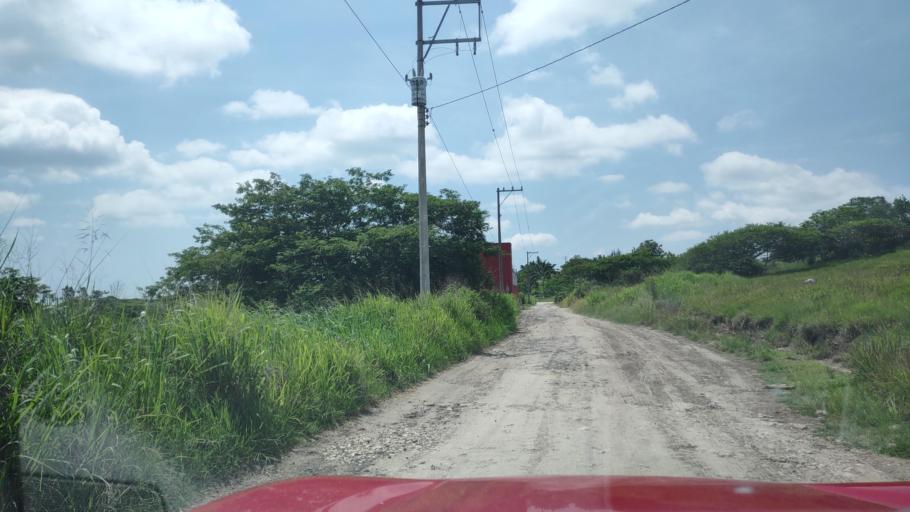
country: MX
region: Veracruz
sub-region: Emiliano Zapata
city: Dos Rios
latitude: 19.4633
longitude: -96.7913
